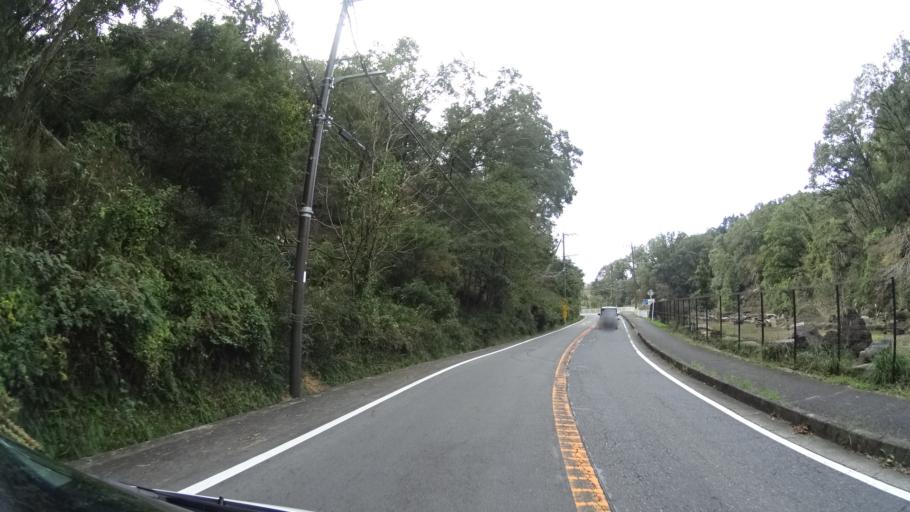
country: JP
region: Shiga Prefecture
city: Otsu-shi
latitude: 35.0380
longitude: 135.8282
